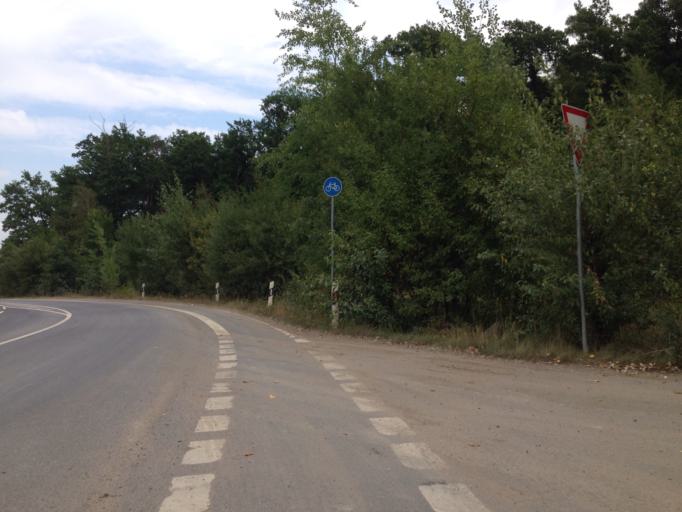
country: DE
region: Hesse
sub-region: Regierungsbezirk Giessen
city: Giessen
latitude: 50.5668
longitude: 8.6935
